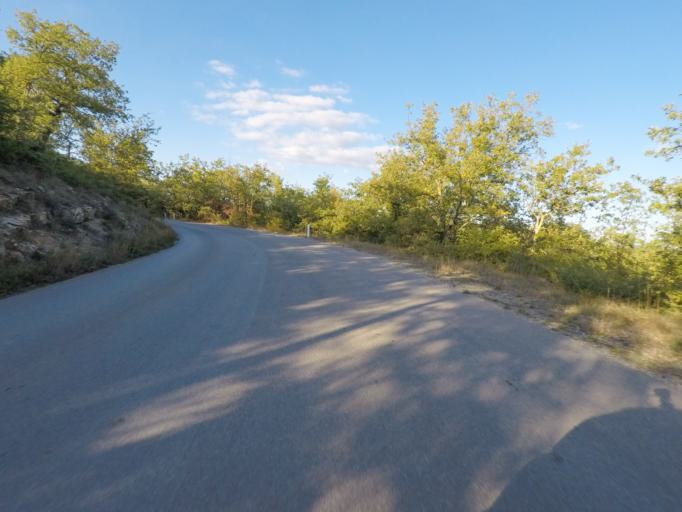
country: IT
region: Tuscany
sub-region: Provincia di Siena
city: Gaiole in Chianti
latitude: 43.4451
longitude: 11.3948
